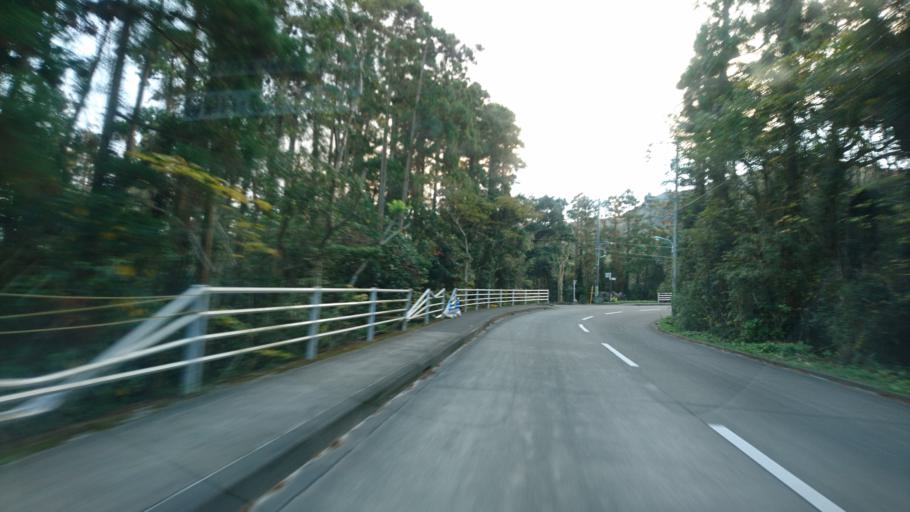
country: JP
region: Shizuoka
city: Shimoda
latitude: 34.3656
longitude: 139.2587
